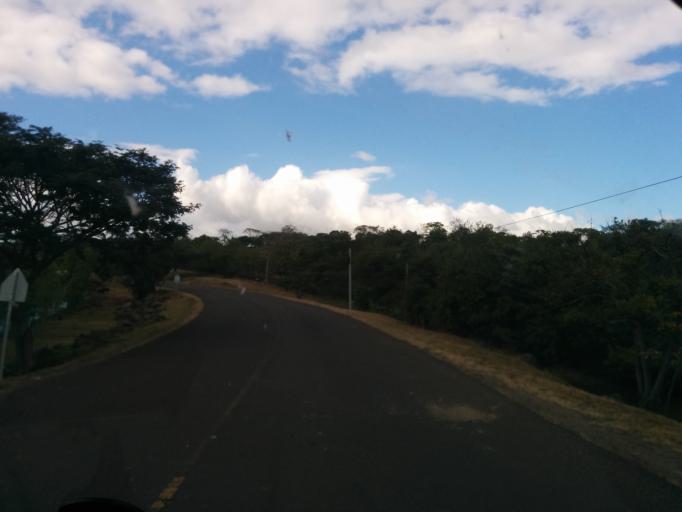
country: NI
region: Esteli
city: Esteli
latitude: 13.1860
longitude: -86.3691
